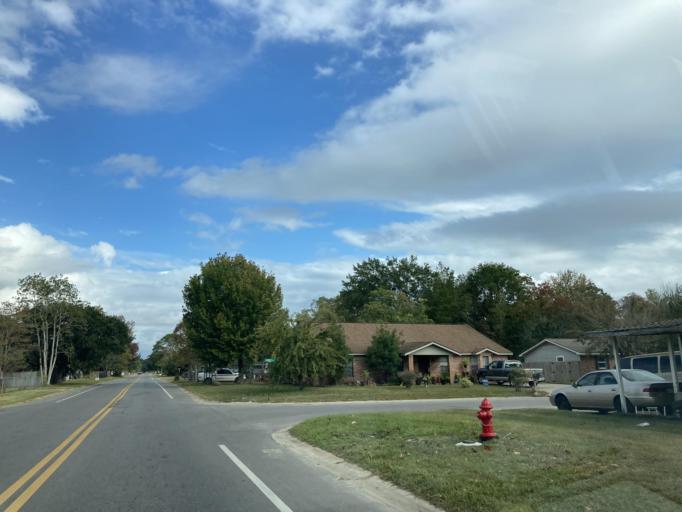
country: US
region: Mississippi
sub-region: Jackson County
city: Gulf Hills
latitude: 30.4360
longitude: -88.8278
